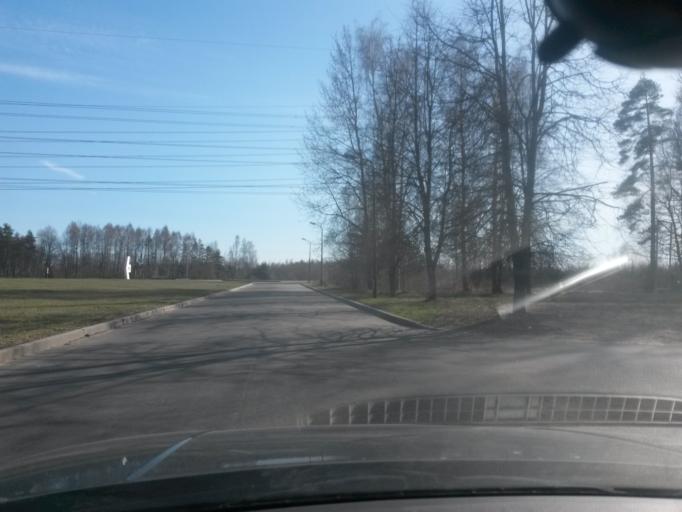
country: LV
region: Stopini
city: Ulbroka
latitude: 56.9157
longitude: 24.2764
